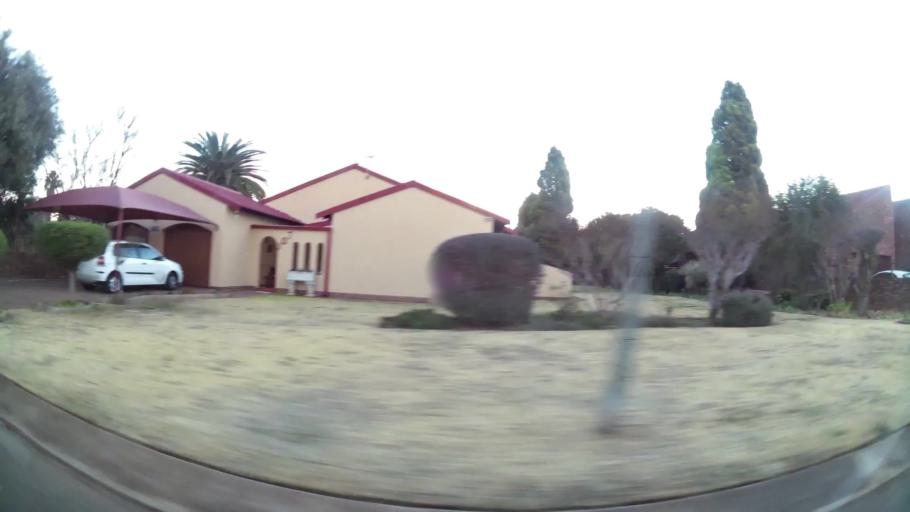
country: ZA
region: North-West
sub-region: Dr Kenneth Kaunda District Municipality
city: Potchefstroom
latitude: -26.7173
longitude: 27.1233
